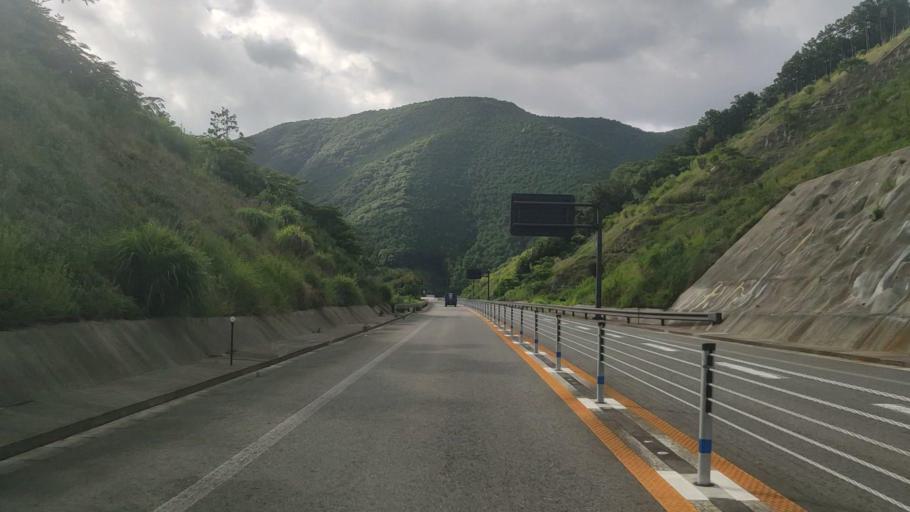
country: JP
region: Wakayama
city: Tanabe
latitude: 33.5585
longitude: 135.5072
